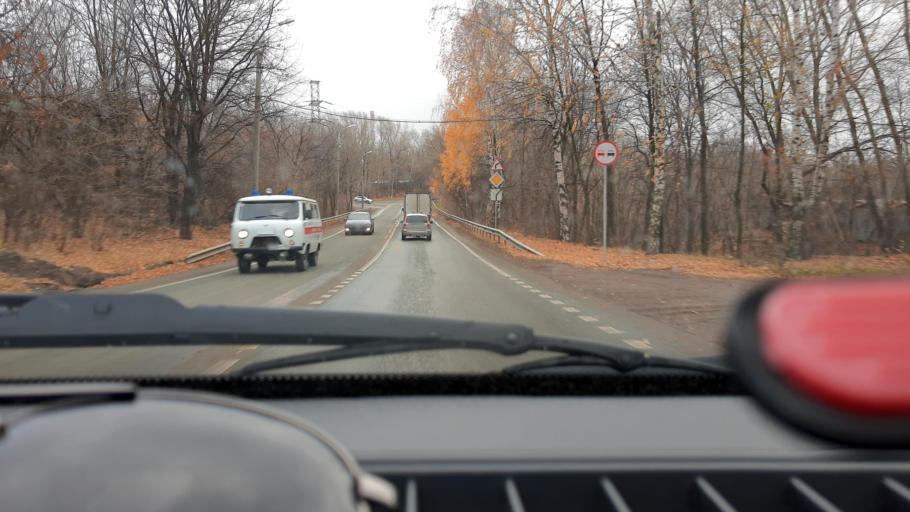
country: RU
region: Bashkortostan
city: Ufa
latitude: 54.8520
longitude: 56.0751
